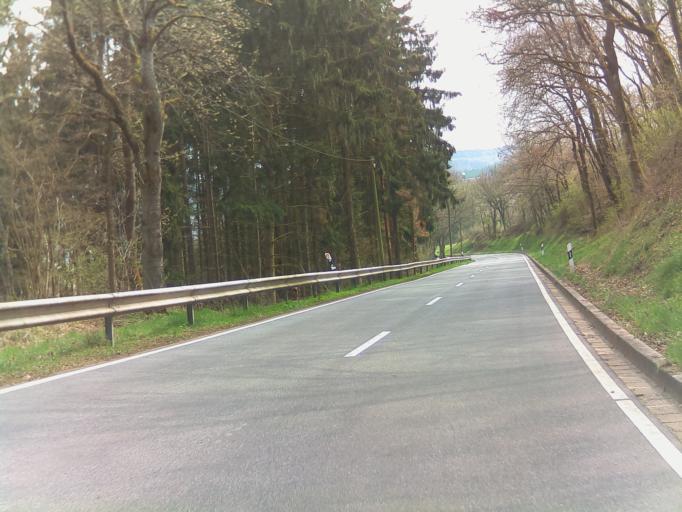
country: DE
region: Rheinland-Pfalz
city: Weitersbach
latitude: 49.8738
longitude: 7.3252
